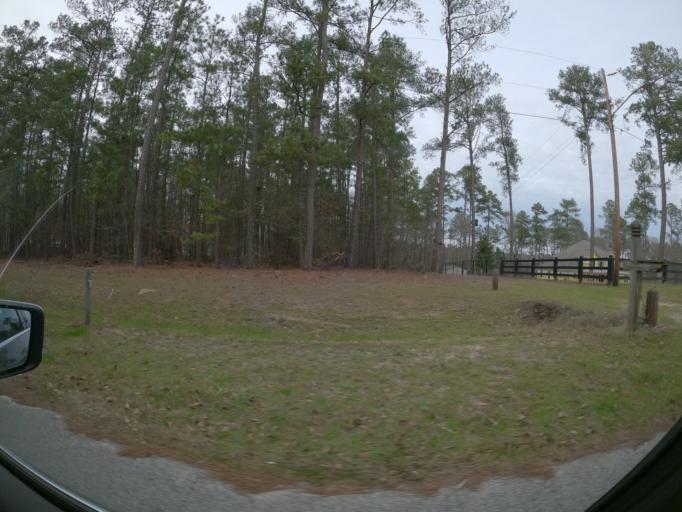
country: US
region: Georgia
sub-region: Columbia County
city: Grovetown
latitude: 33.4627
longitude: -82.1972
